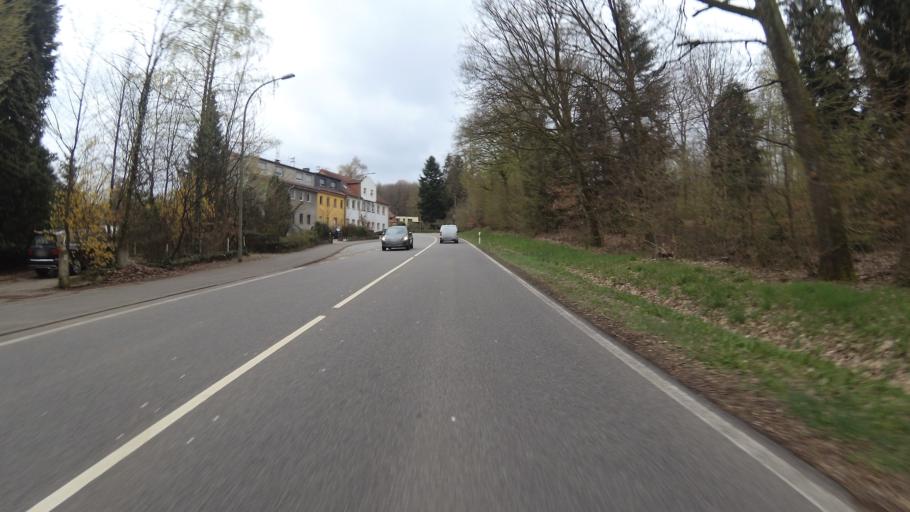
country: DE
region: Saarland
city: Friedrichsthal
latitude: 49.3427
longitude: 7.0750
